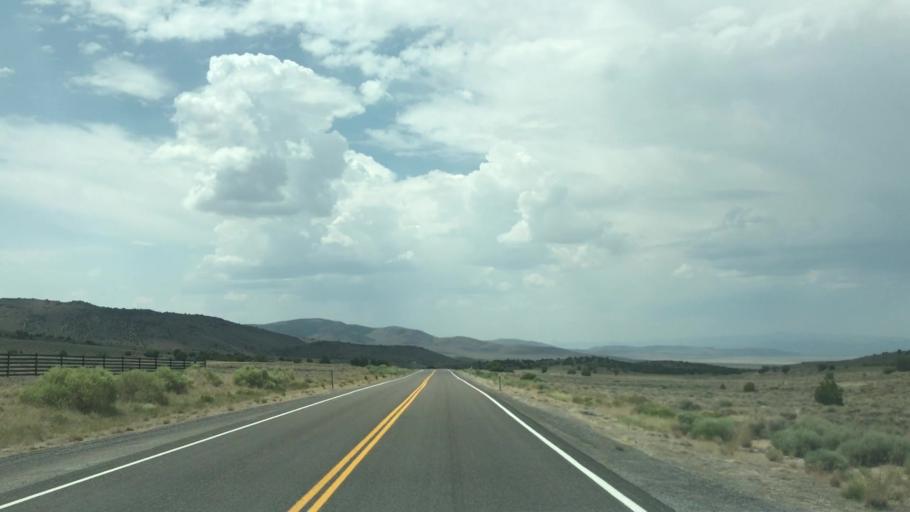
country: US
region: Nevada
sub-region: Eureka County
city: Eureka
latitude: 39.4091
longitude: -115.6968
